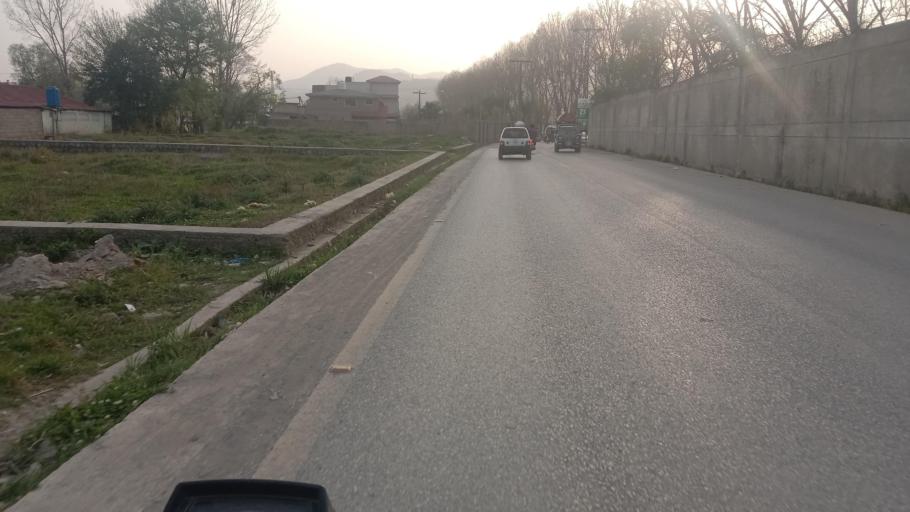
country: PK
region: Khyber Pakhtunkhwa
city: Abbottabad
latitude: 34.1738
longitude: 73.2387
